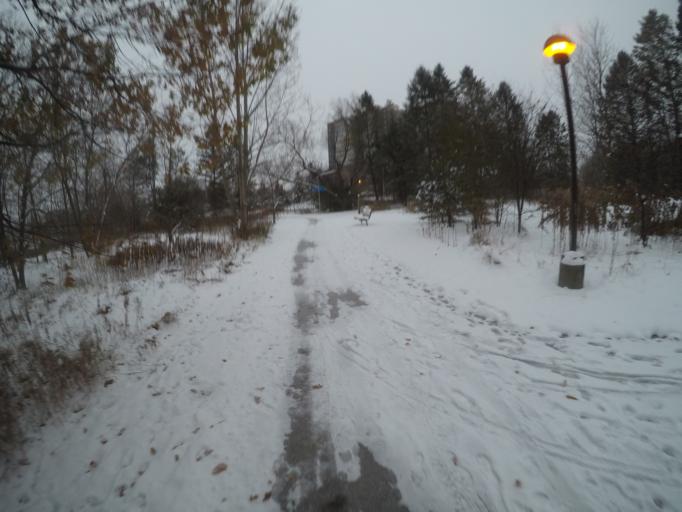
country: CA
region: Ontario
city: Waterloo
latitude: 43.4852
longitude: -80.5052
